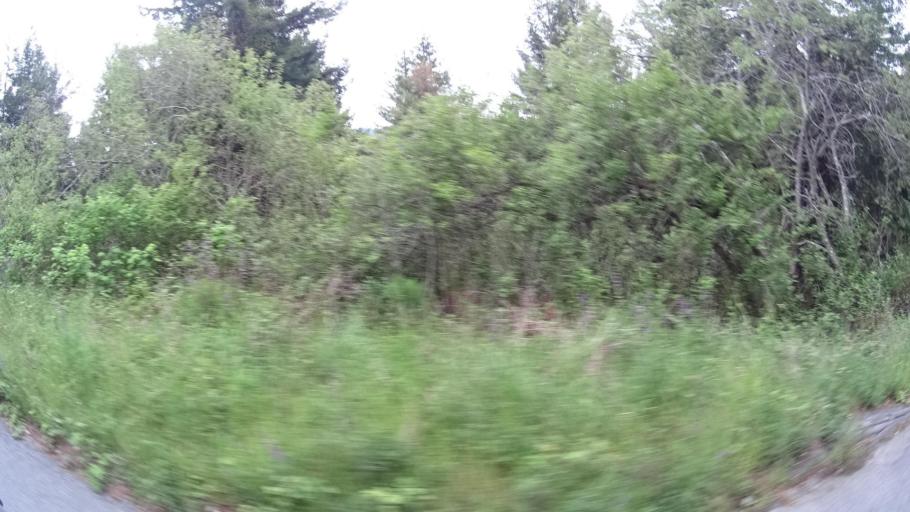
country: US
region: California
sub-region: Humboldt County
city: Blue Lake
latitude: 40.8726
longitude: -123.9716
